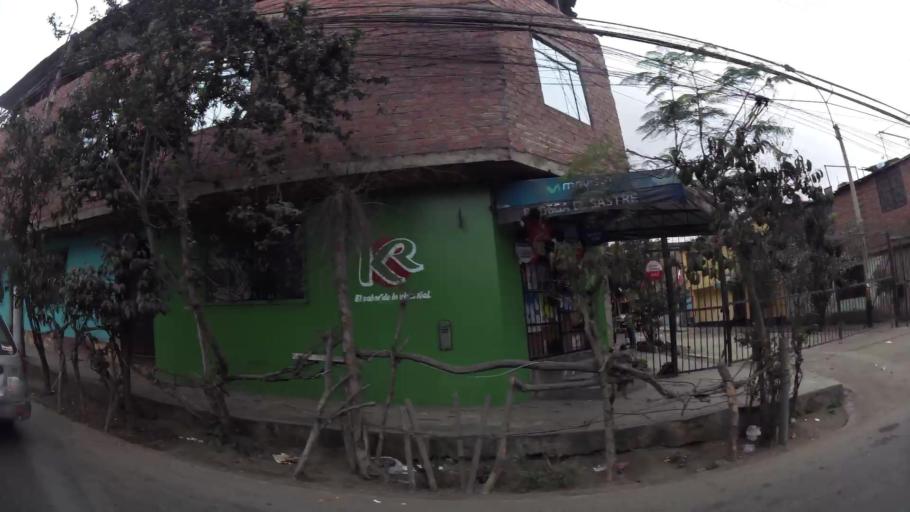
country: PE
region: Lima
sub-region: Lima
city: Surco
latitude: -12.1441
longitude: -76.9681
